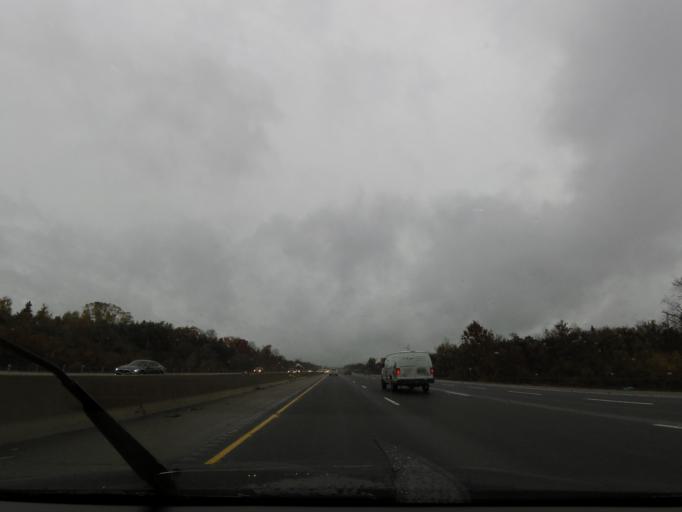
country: CA
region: Ontario
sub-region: Wellington County
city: Guelph
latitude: 43.4459
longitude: -80.1869
